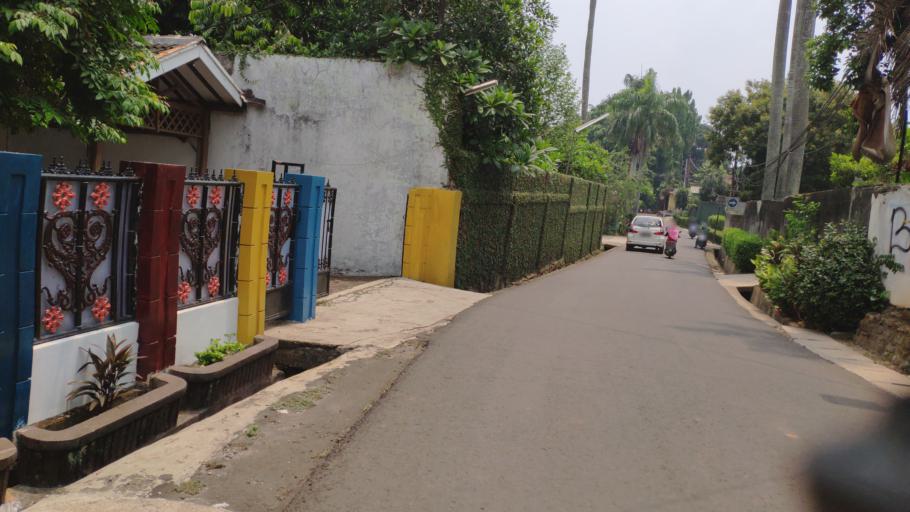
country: ID
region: West Java
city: Depok
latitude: -6.3188
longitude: 106.8307
